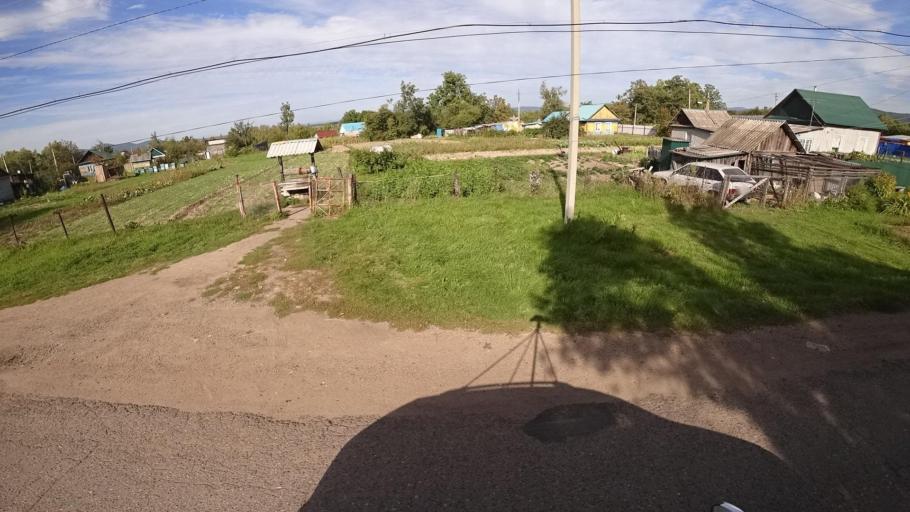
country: RU
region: Primorskiy
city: Dostoyevka
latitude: 44.3006
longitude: 133.4495
